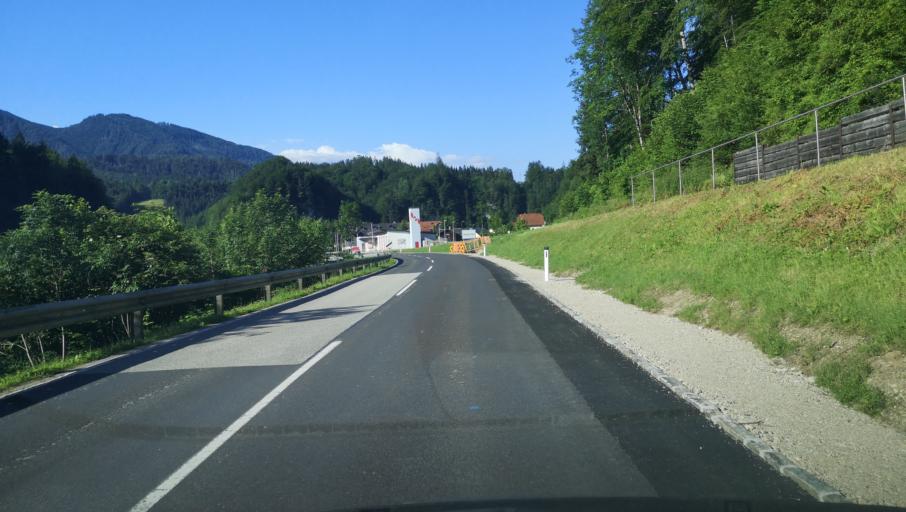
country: AT
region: Lower Austria
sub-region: Politischer Bezirk Amstetten
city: Opponitz
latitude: 47.8851
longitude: 14.8235
